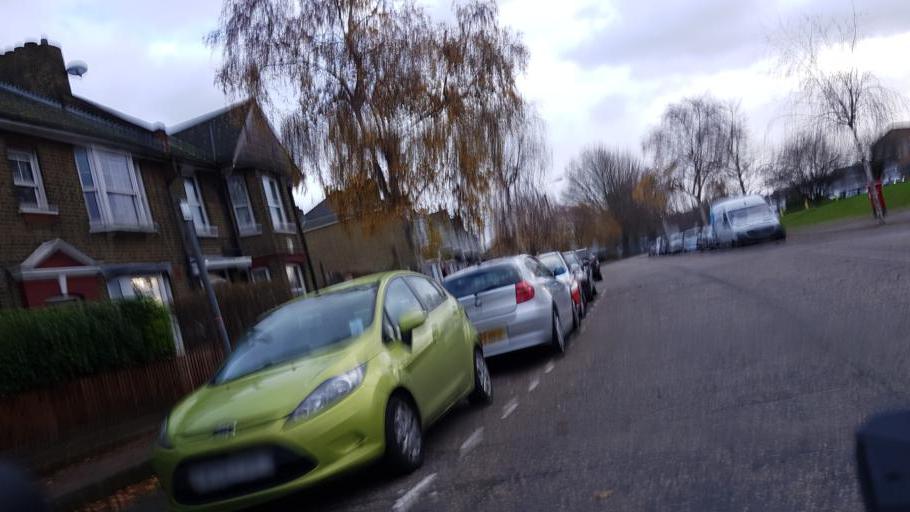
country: GB
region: England
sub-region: Greater London
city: Woolwich
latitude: 51.4921
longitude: 0.0298
